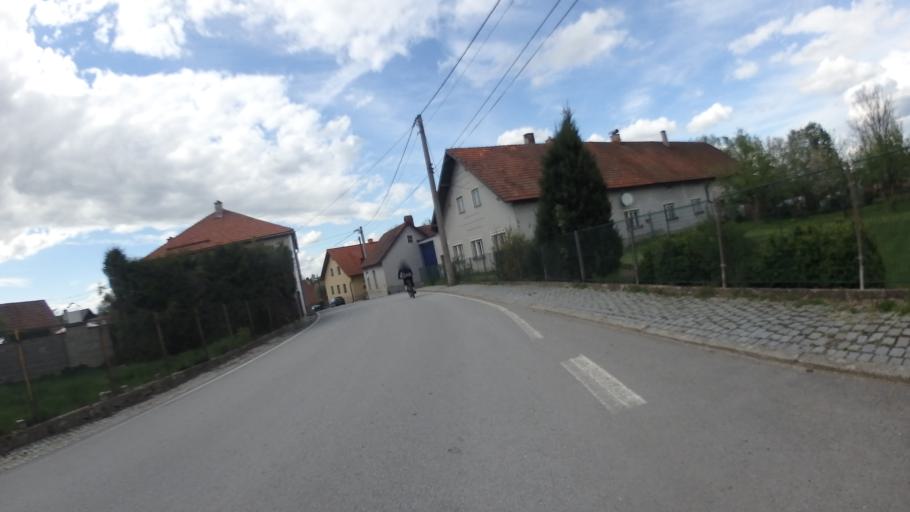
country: CZ
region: Vysocina
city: Merin
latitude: 49.3619
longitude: 15.9091
